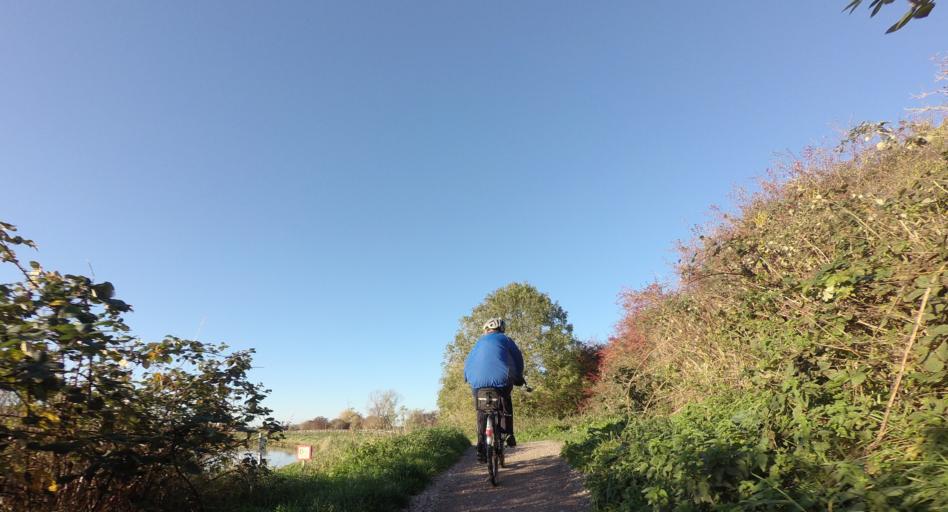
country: GB
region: England
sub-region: West Sussex
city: Steyning
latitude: 50.8681
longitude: -0.2981
